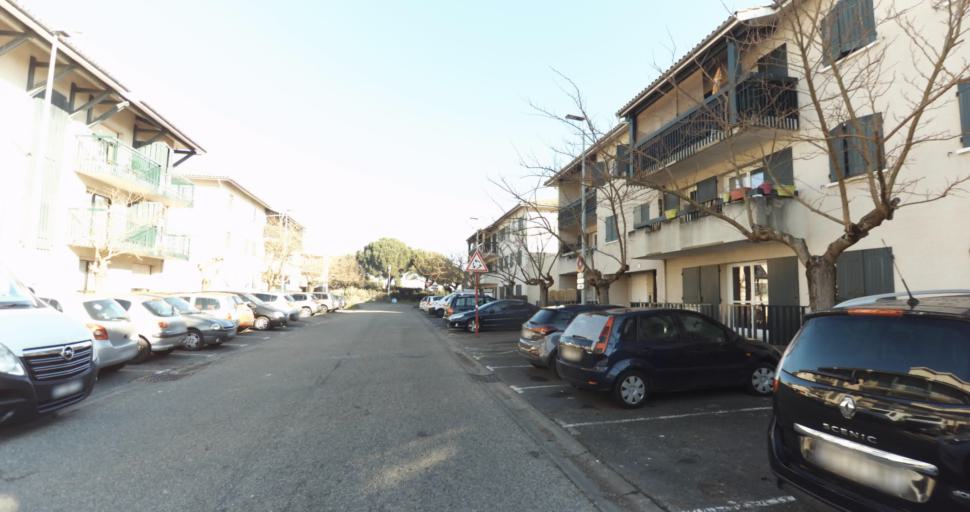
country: FR
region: Aquitaine
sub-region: Departement de la Gironde
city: Carbon-Blanc
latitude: 44.8965
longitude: -0.5018
